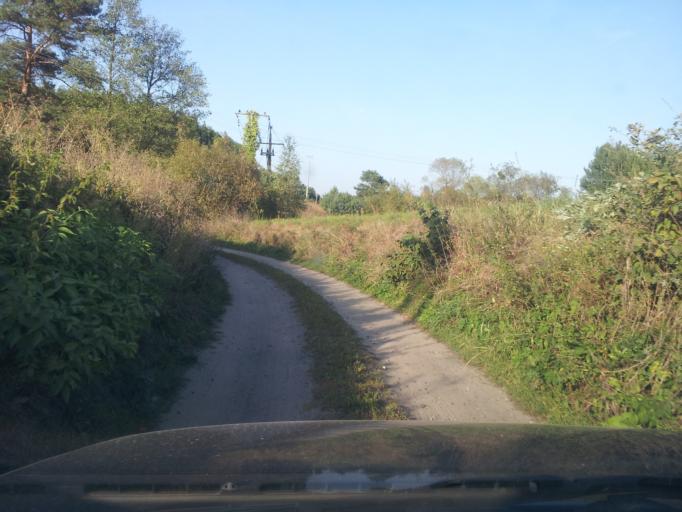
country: PL
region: Kujawsko-Pomorskie
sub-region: Powiat brodnicki
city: Gorzno
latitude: 53.2130
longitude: 19.6498
